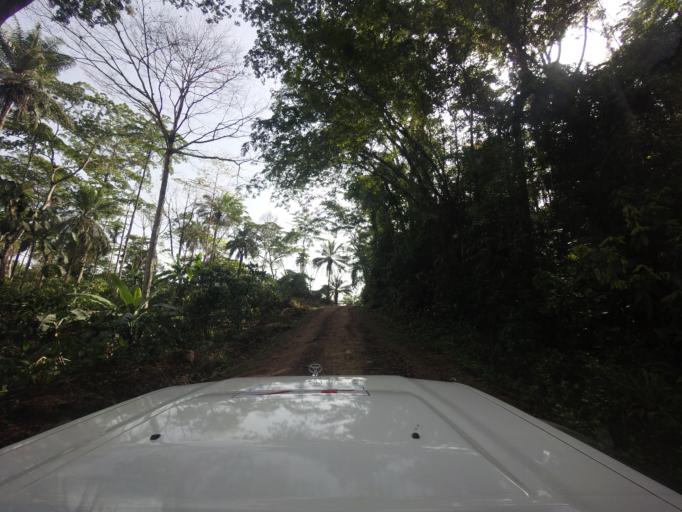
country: LR
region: Lofa
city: Voinjama
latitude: 8.5174
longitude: -9.7614
